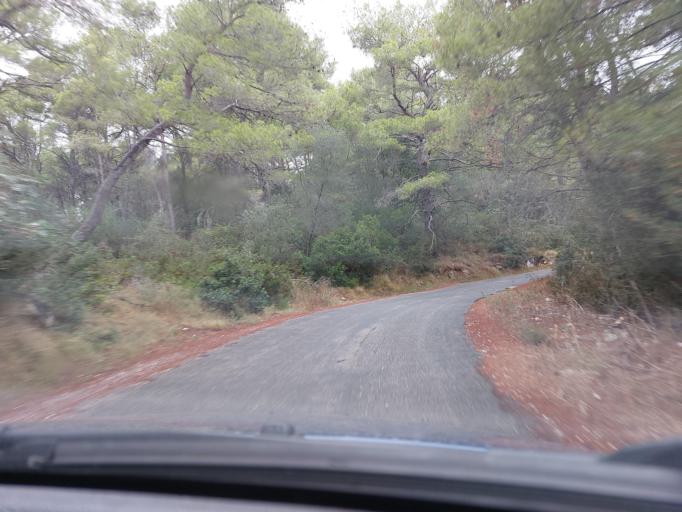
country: HR
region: Dubrovacko-Neretvanska
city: Smokvica
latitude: 42.7636
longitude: 16.9003
